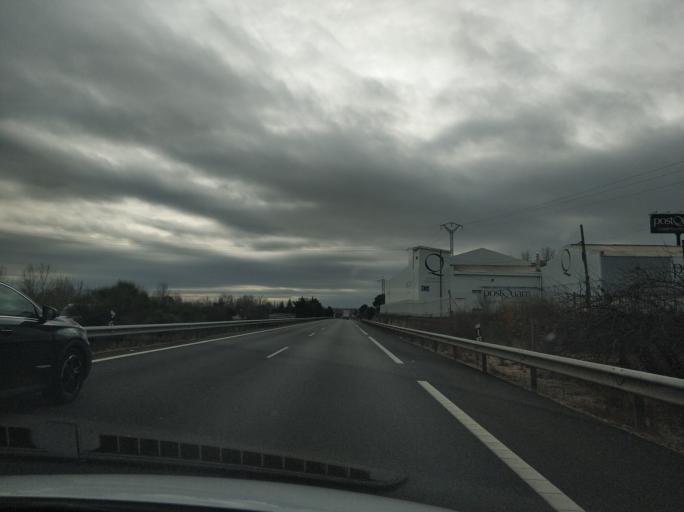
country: ES
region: Castille and Leon
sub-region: Provincia de Valladolid
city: Santovenia de Pisuerga
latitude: 41.7240
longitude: -4.6896
